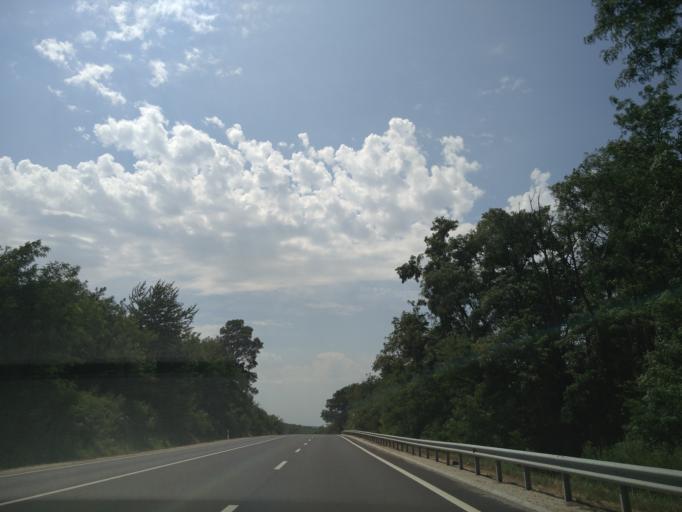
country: HU
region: Vas
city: Vasvar
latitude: 47.0664
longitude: 16.8335
